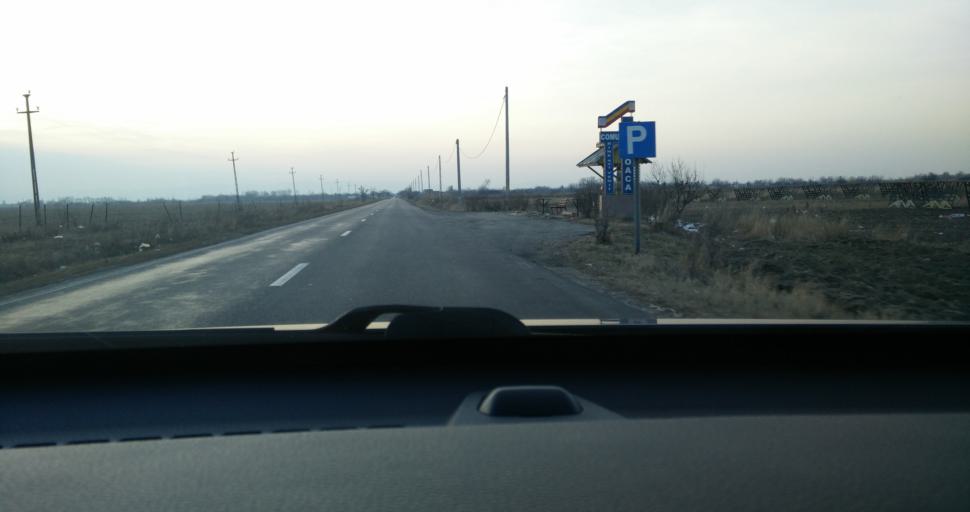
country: RO
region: Vrancea
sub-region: Comuna Rastoaca
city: Rastoaca
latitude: 45.6518
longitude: 27.3097
